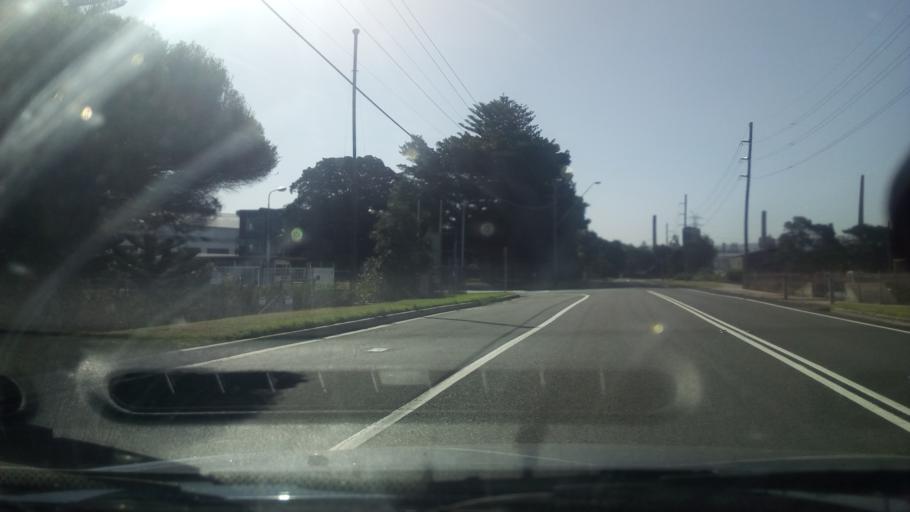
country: AU
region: New South Wales
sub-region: Wollongong
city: Port Kembla
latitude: -34.4747
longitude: 150.9020
